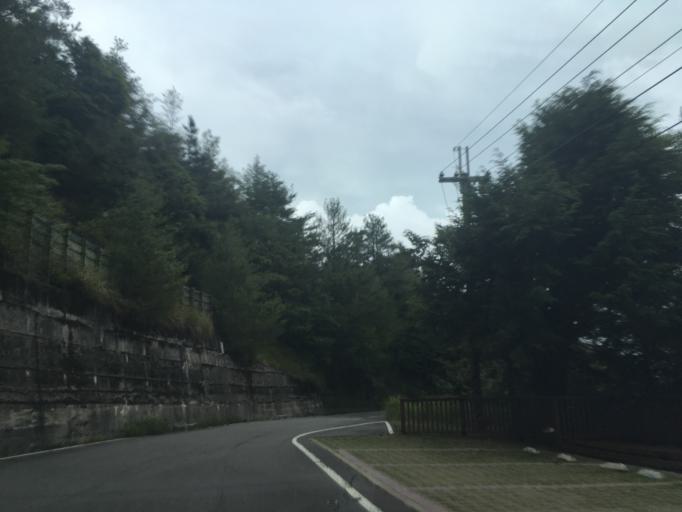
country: TW
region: Taiwan
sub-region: Nantou
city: Puli
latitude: 24.2737
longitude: 121.0326
